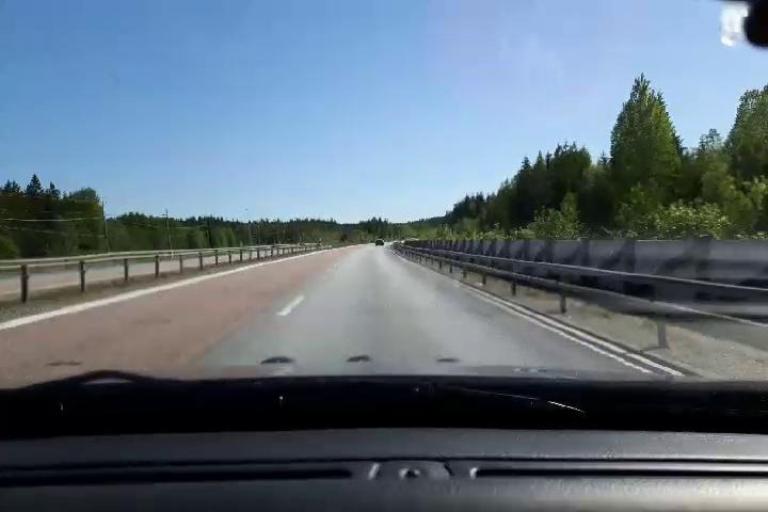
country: SE
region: Gaevleborg
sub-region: Soderhamns Kommun
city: Soderhamn
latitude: 61.4063
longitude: 16.9939
